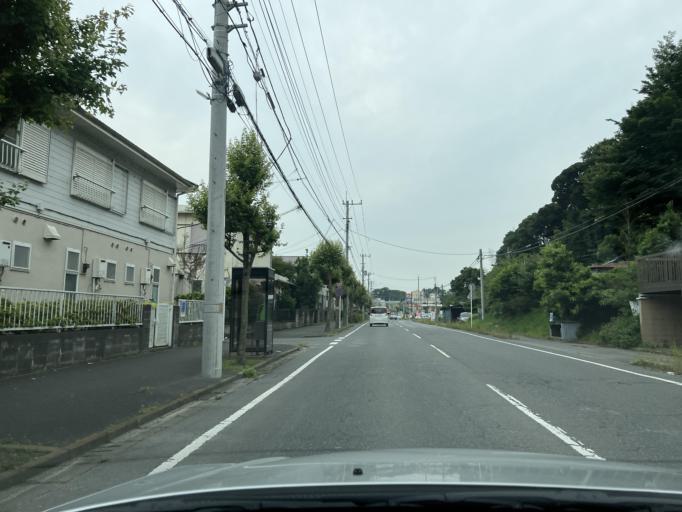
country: JP
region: Chiba
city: Nagareyama
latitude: 35.8471
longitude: 139.9147
